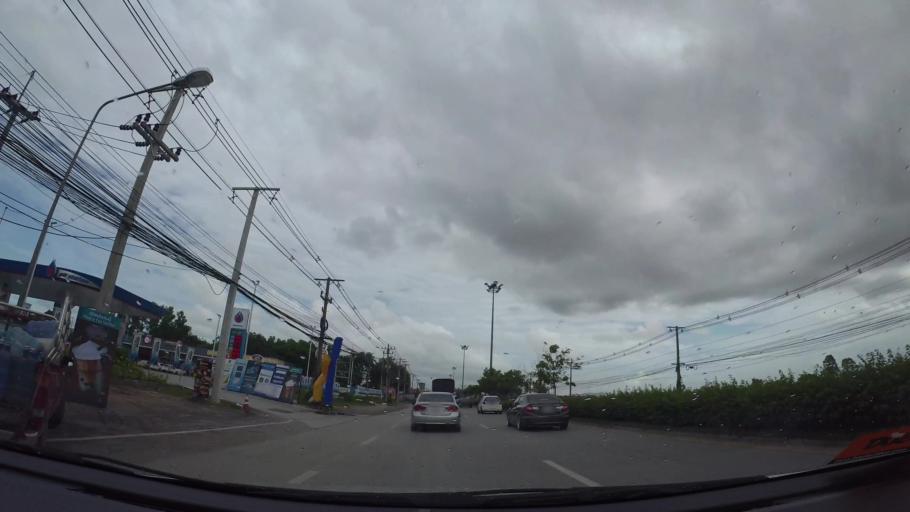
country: TH
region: Rayong
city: Rayong
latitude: 12.6966
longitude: 101.1963
